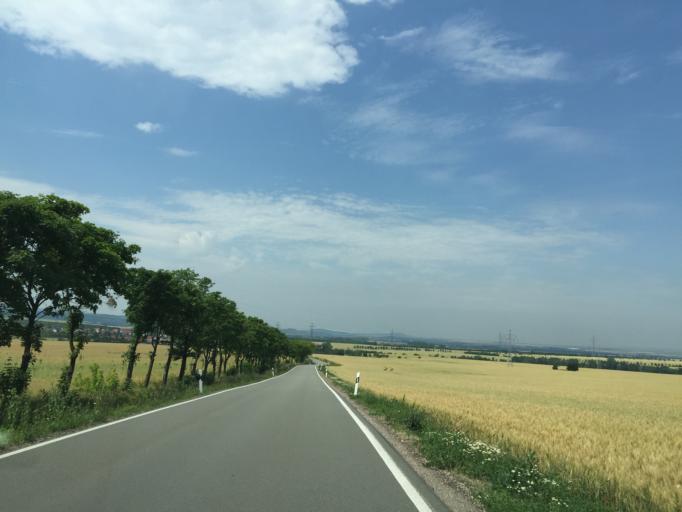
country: DE
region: Thuringia
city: Alkersleben
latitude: 50.8207
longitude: 11.0343
